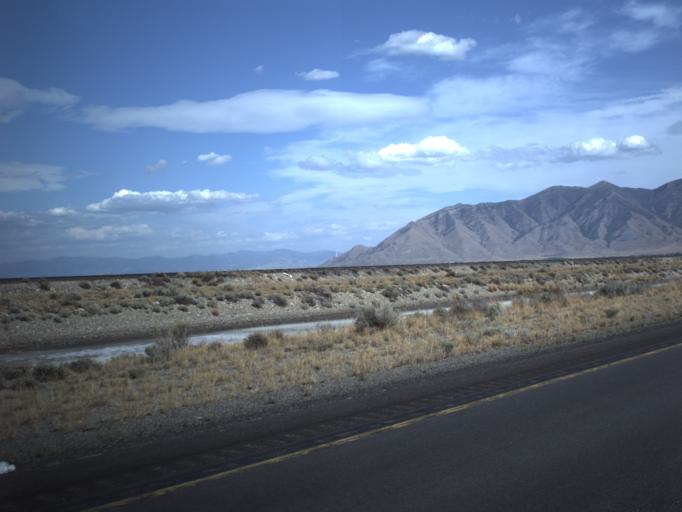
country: US
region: Utah
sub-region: Tooele County
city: Grantsville
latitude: 40.6751
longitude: -112.4019
